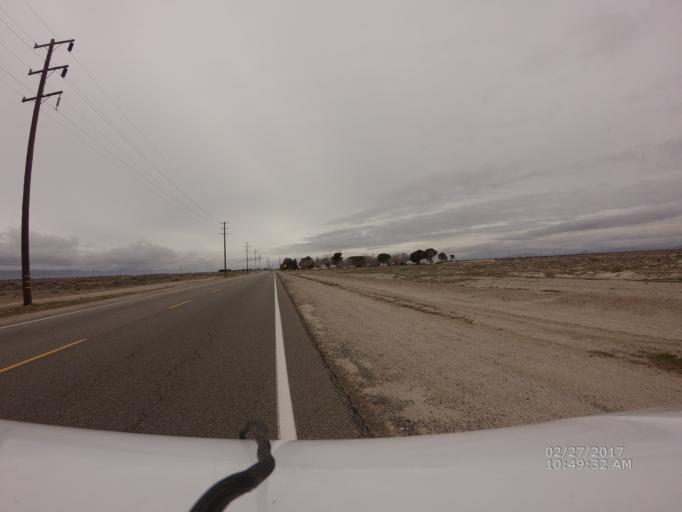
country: US
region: California
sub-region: Los Angeles County
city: Lancaster
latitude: 34.7627
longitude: -118.1424
